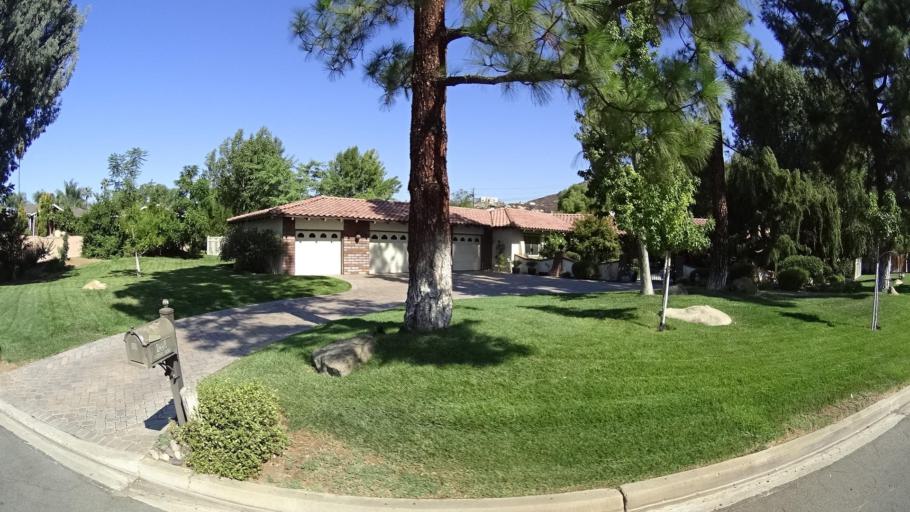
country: US
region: California
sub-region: San Diego County
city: Granite Hills
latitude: 32.7907
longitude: -116.8957
